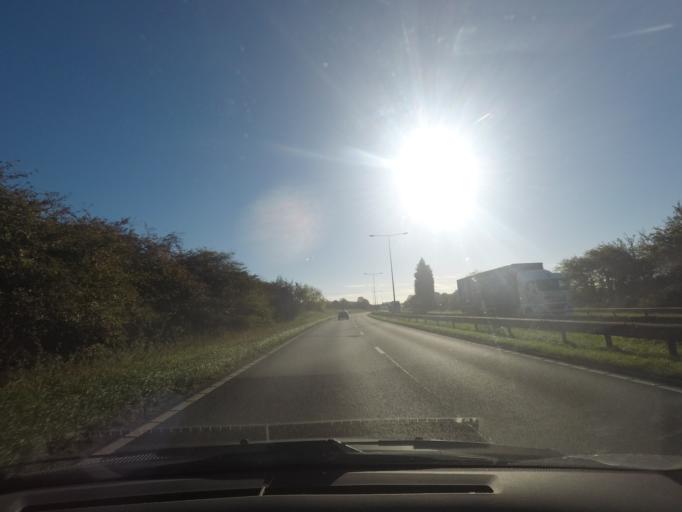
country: GB
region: England
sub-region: East Riding of Yorkshire
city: South Cave
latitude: 53.7595
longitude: -0.5912
